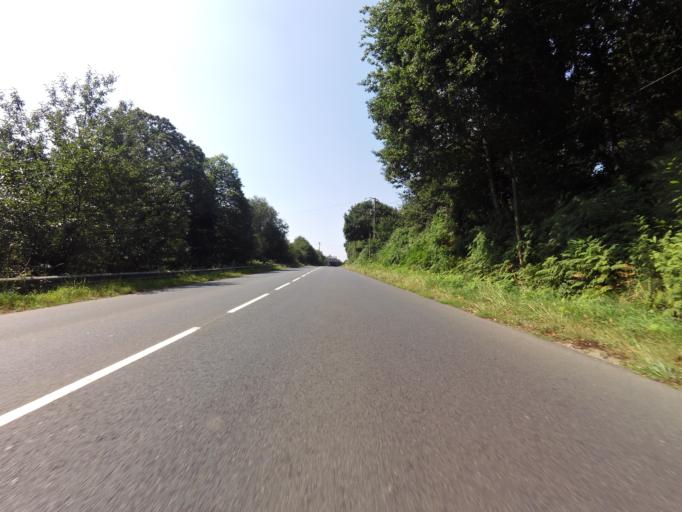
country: FR
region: Brittany
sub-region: Departement du Finistere
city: Pluguffan
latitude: 47.9502
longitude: -4.1951
